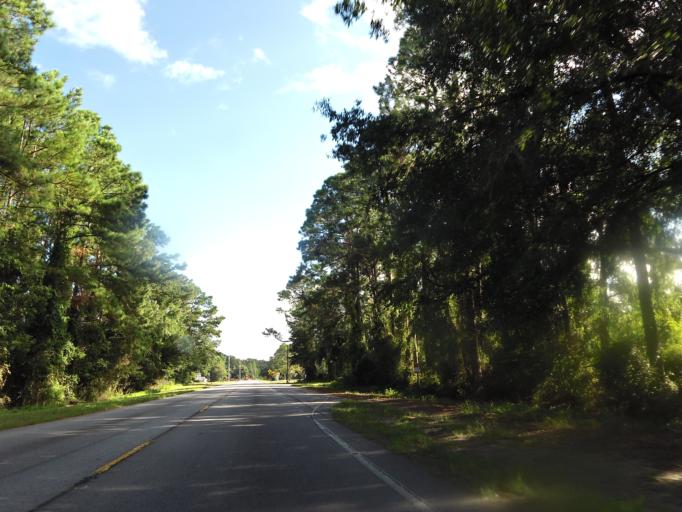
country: US
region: Georgia
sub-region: Glynn County
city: Country Club Estates
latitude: 31.2412
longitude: -81.4508
